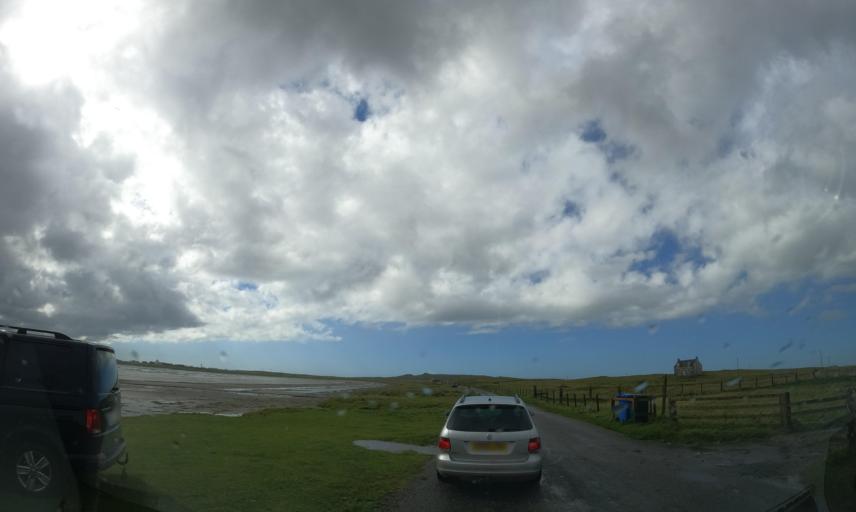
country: GB
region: Scotland
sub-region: Eilean Siar
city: Barra
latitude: 56.5192
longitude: -6.8115
